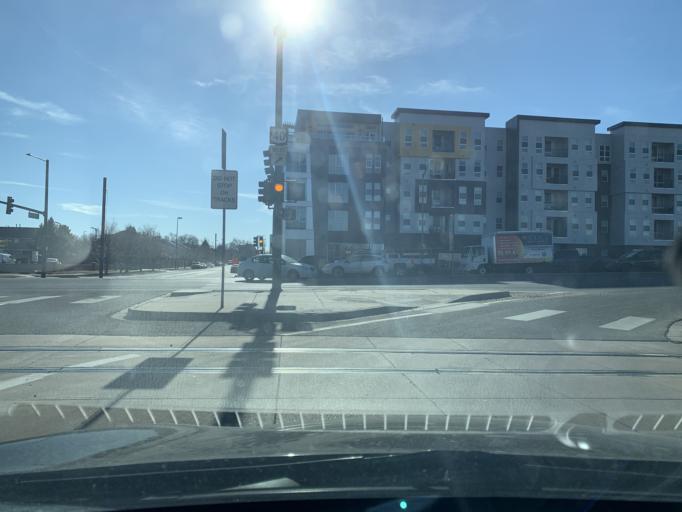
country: US
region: Colorado
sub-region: Denver County
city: Denver
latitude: 39.7408
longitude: -105.0054
